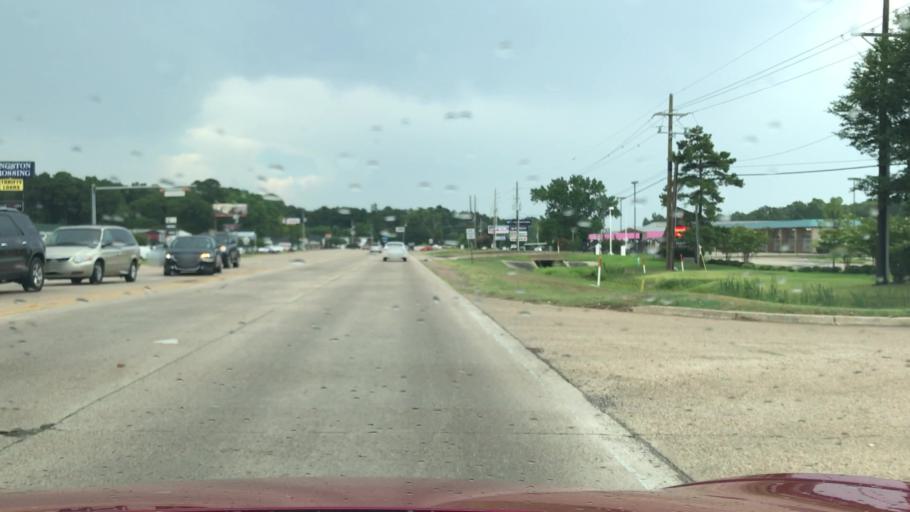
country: US
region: Louisiana
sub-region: Bossier Parish
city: Bossier City
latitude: 32.4014
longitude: -93.7800
